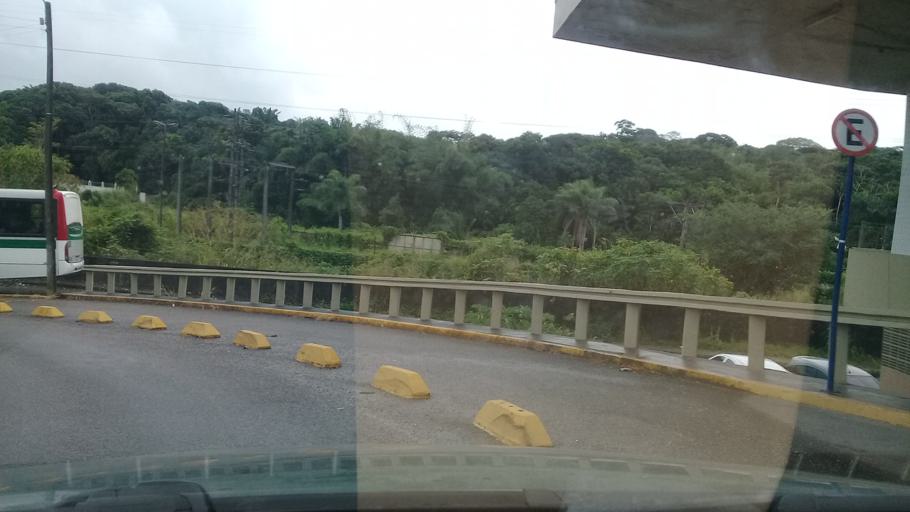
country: BR
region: Pernambuco
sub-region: Jaboatao Dos Guararapes
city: Jaboatao dos Guararapes
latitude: -8.0635
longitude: -34.9817
